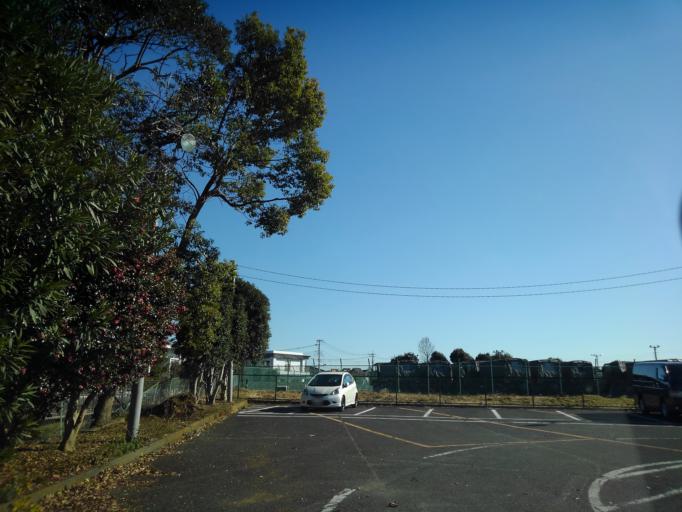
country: JP
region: Tokyo
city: Fussa
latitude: 35.7678
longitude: 139.3318
